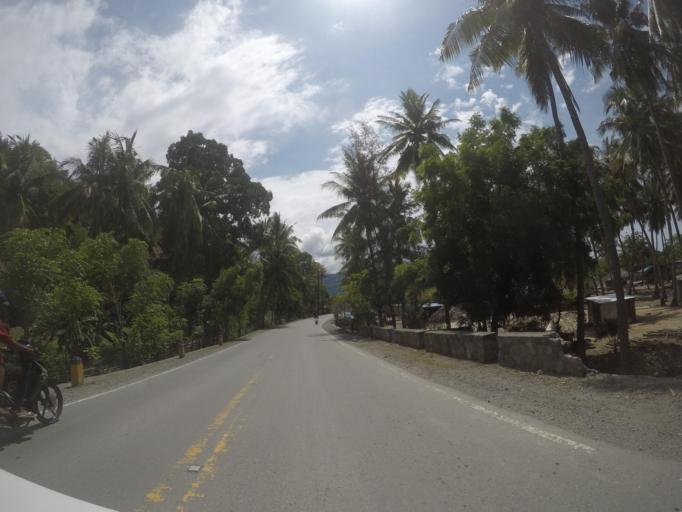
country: TL
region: Dili
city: Dili
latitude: -8.5697
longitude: 125.4664
